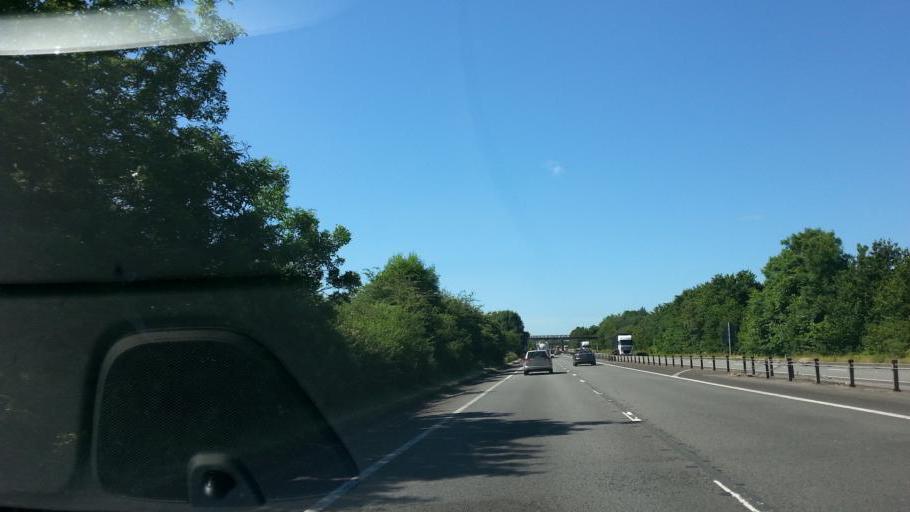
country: GB
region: Wales
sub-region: Monmouthshire
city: Usk
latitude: 51.7088
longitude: -2.8675
